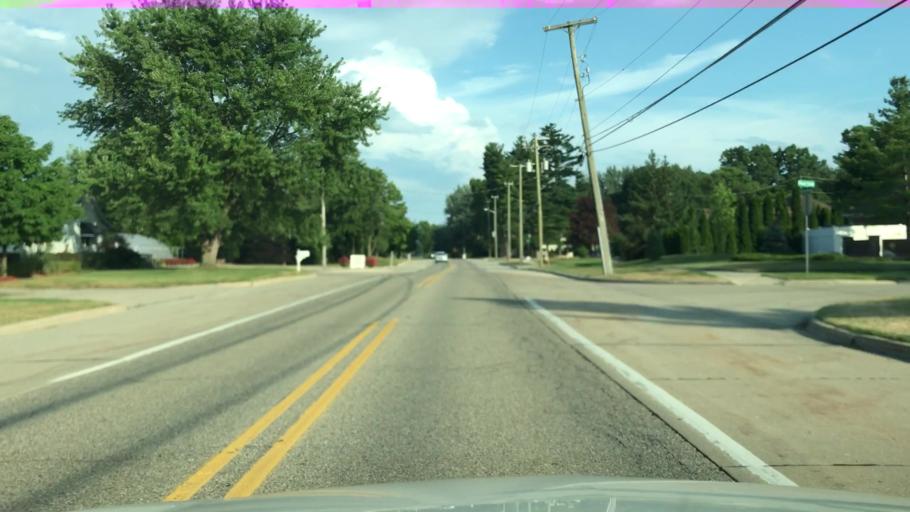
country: US
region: Michigan
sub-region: Macomb County
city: Sterling Heights
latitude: 42.5844
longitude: -82.9775
